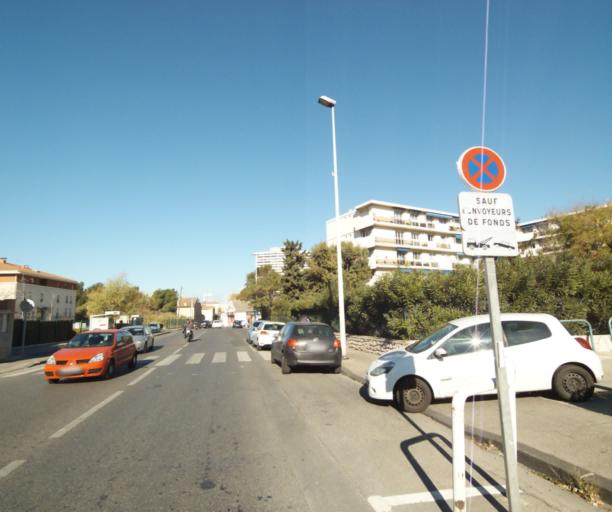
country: FR
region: Provence-Alpes-Cote d'Azur
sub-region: Departement des Bouches-du-Rhone
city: Marseille 09
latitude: 43.2608
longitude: 5.3939
